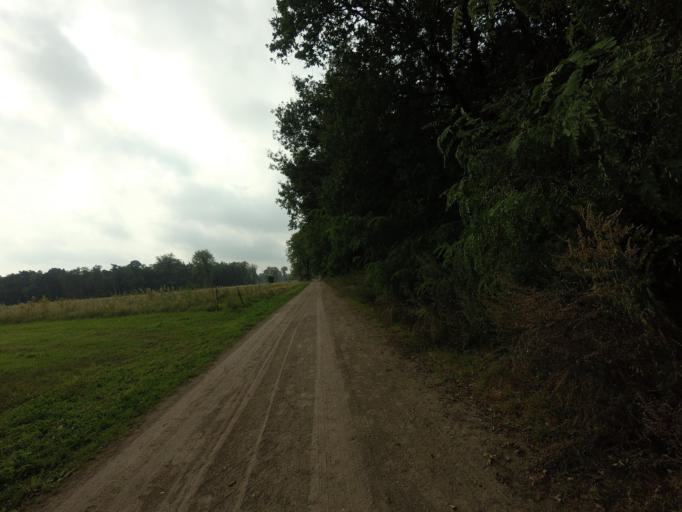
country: DE
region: Lower Saxony
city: Getelo
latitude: 52.4381
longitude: 6.8725
